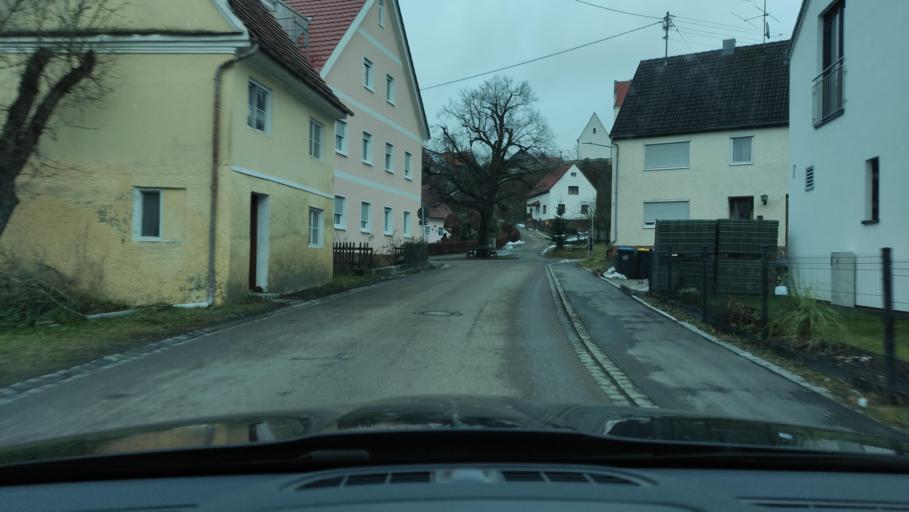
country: DE
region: Bavaria
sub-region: Swabia
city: Deisenhausen
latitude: 48.2746
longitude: 10.3302
